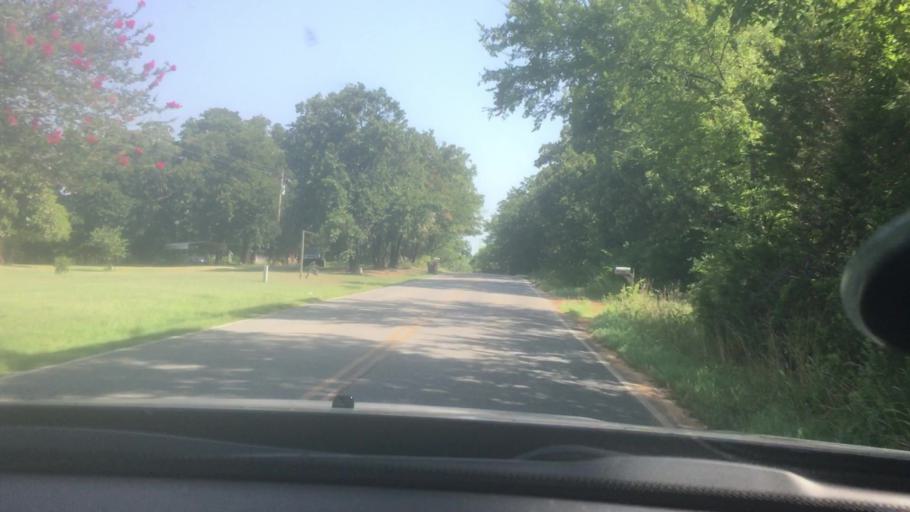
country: US
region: Oklahoma
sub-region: Bryan County
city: Durant
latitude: 34.0442
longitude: -96.4743
